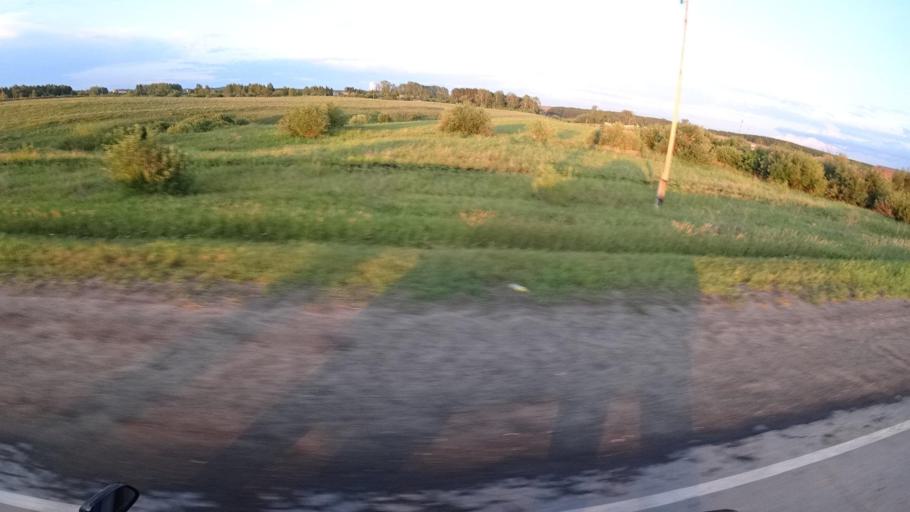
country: RU
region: Sverdlovsk
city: Kamyshlov
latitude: 56.8726
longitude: 62.7116
